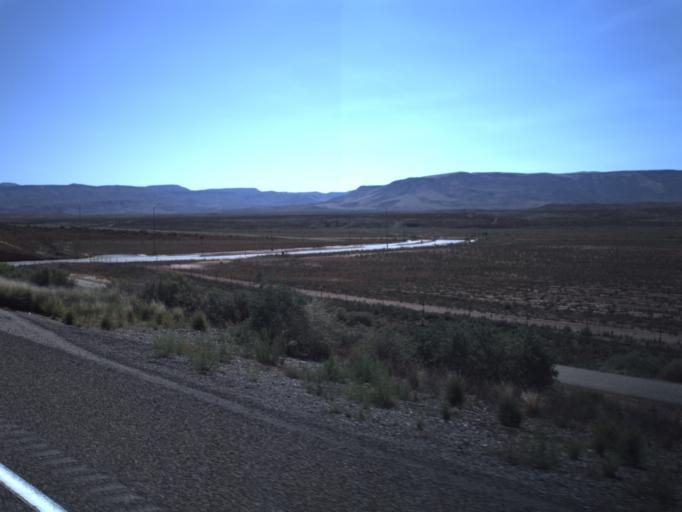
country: US
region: Utah
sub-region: Washington County
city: Saint George
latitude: 37.0264
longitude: -113.6030
